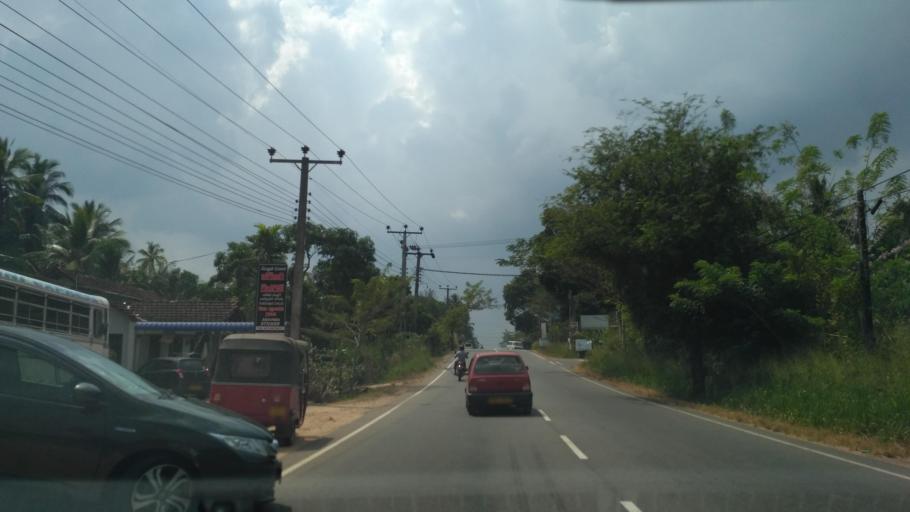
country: LK
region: North Western
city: Kuliyapitiya
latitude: 7.3262
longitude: 80.1139
